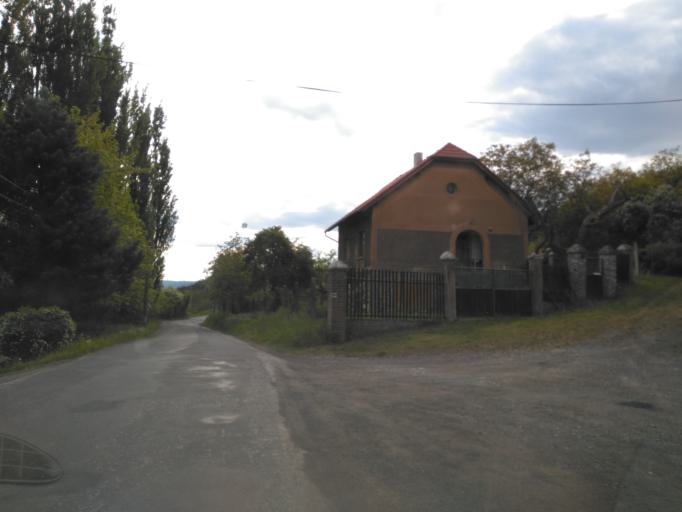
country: CZ
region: Central Bohemia
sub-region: Okres Beroun
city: Kraluv Dvur
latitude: 49.9154
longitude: 14.0200
